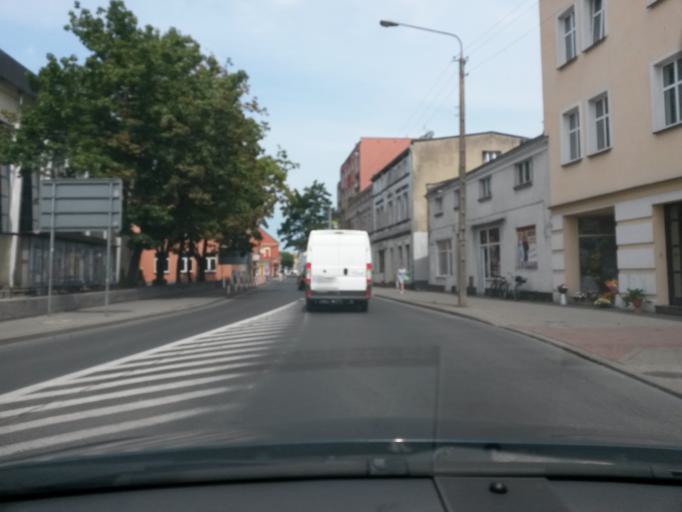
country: PL
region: Greater Poland Voivodeship
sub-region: Powiat gostynski
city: Gostyn
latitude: 51.8775
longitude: 17.0118
